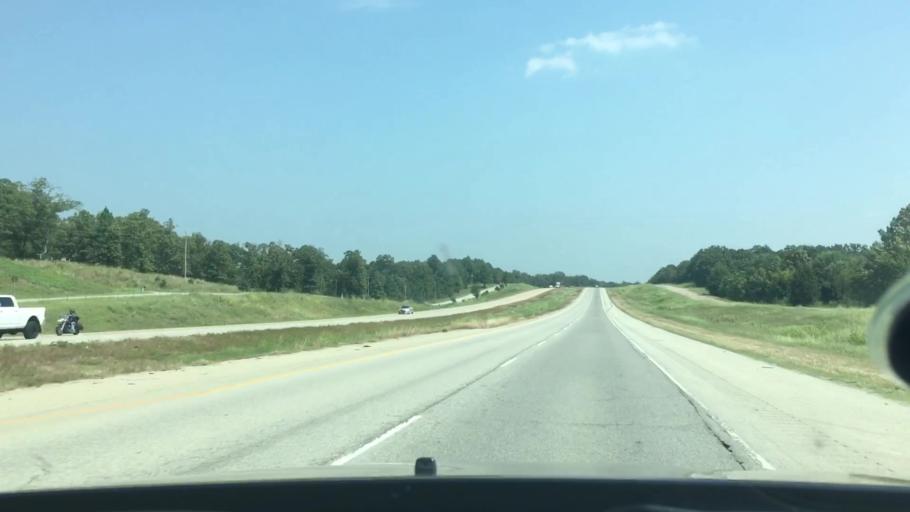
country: US
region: Oklahoma
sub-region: Atoka County
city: Atoka
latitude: 34.2886
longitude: -96.1955
